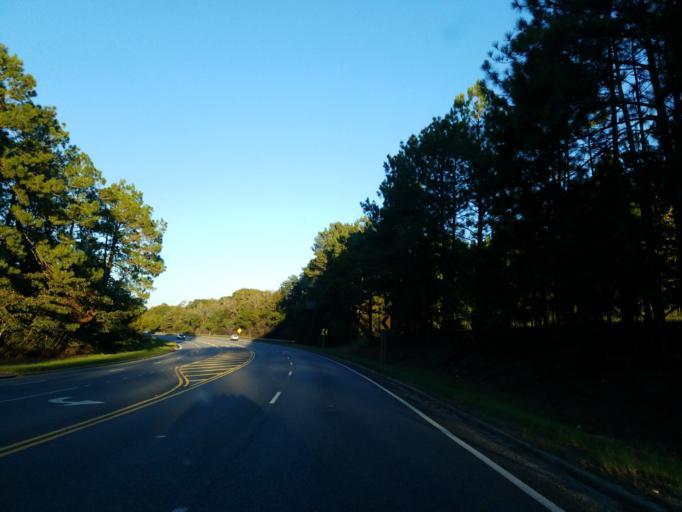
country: US
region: Georgia
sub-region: Tift County
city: Unionville
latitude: 31.4378
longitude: -83.5647
